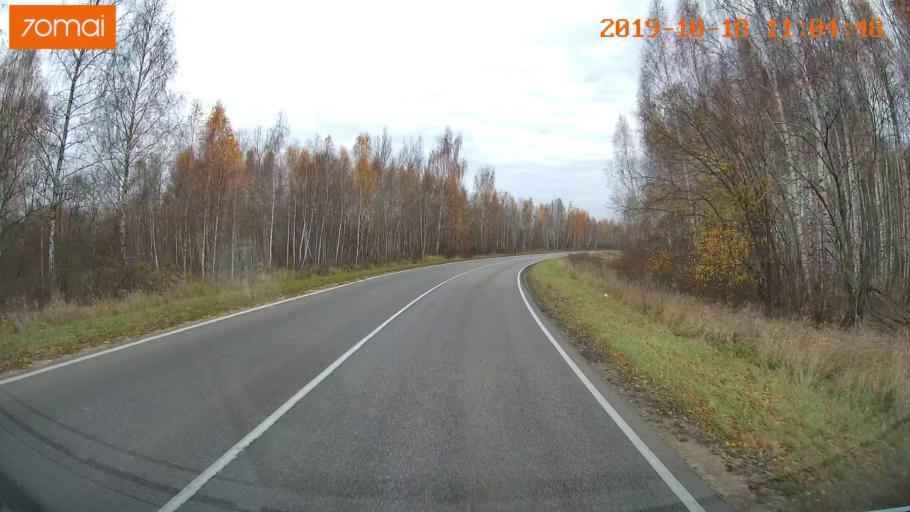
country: RU
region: Tula
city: Yepifan'
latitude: 53.8975
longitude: 38.5419
